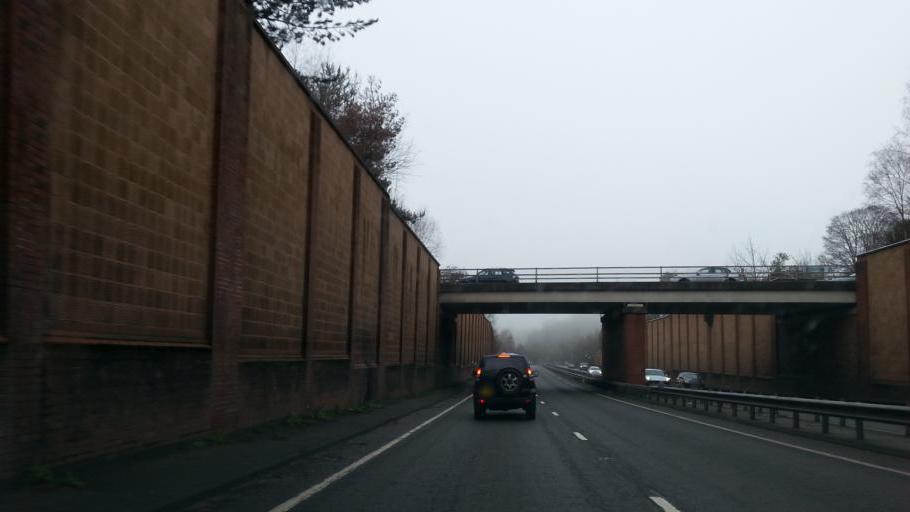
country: GB
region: England
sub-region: Cheshire East
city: Wilmslow
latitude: 53.3254
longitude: -2.2254
